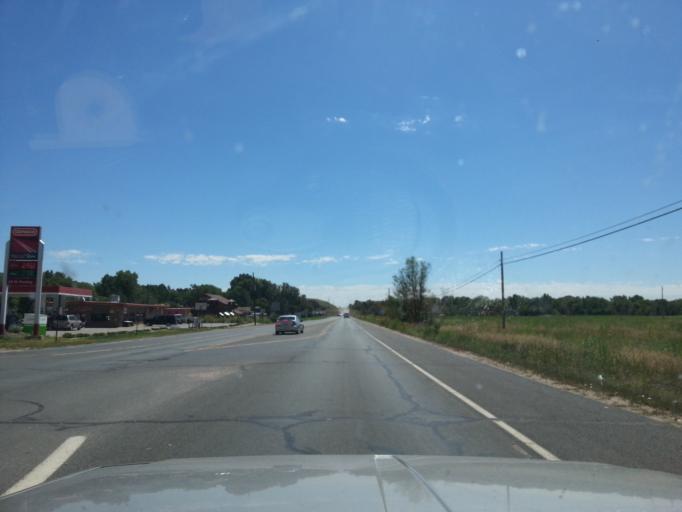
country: US
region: Colorado
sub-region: Larimer County
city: Loveland
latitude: 40.4100
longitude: -105.1623
